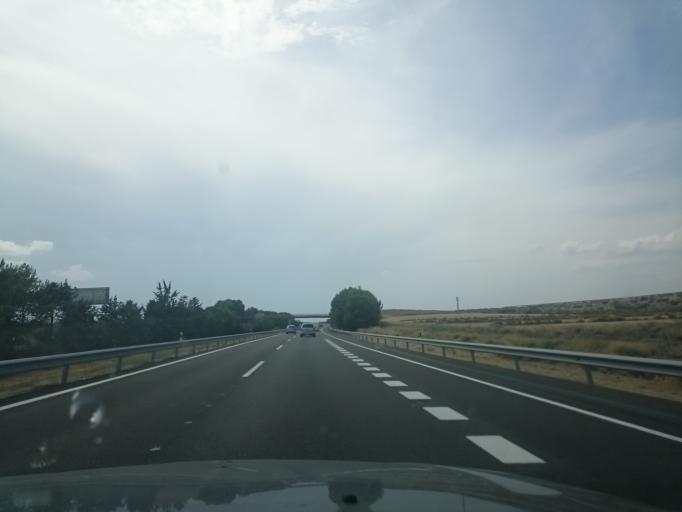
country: ES
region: Aragon
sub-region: Provincia de Zaragoza
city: Bujaraloz
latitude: 41.5251
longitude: -0.1816
